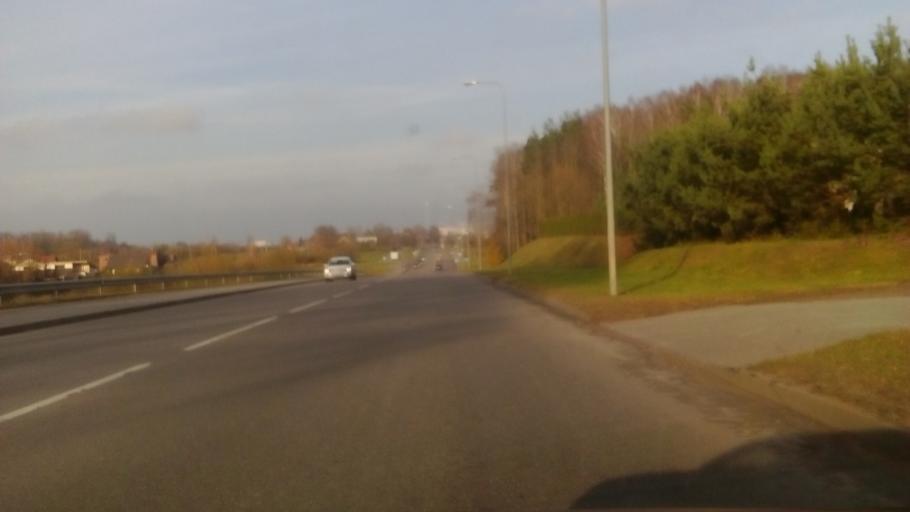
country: LT
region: Alytaus apskritis
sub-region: Alytus
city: Alytus
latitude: 54.4017
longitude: 24.0015
